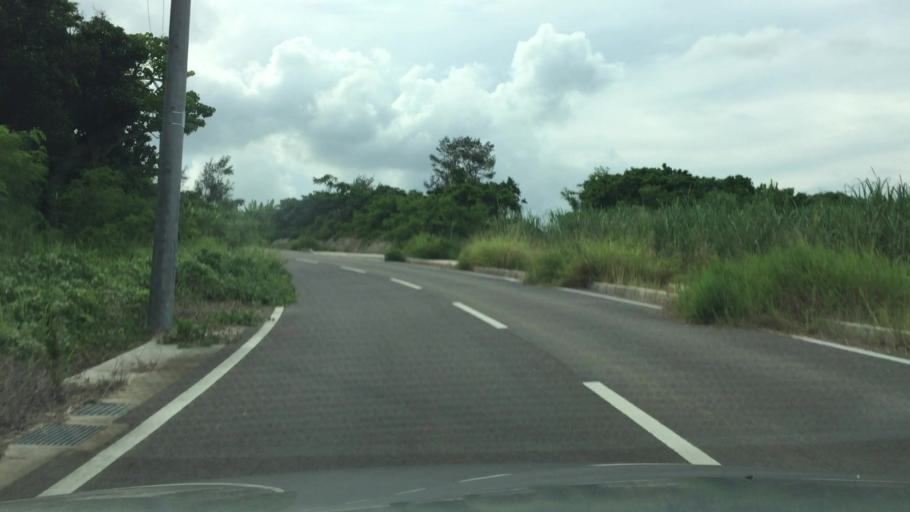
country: JP
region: Okinawa
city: Ishigaki
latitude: 24.4680
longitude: 124.1398
